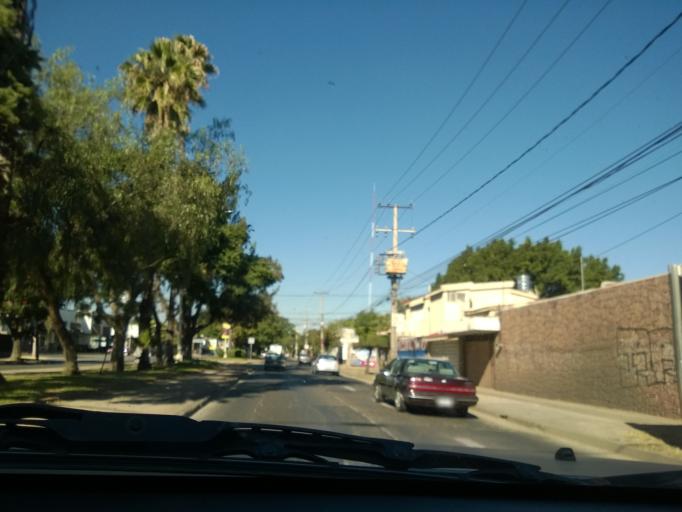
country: MX
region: Guanajuato
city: Leon
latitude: 21.1086
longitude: -101.6641
